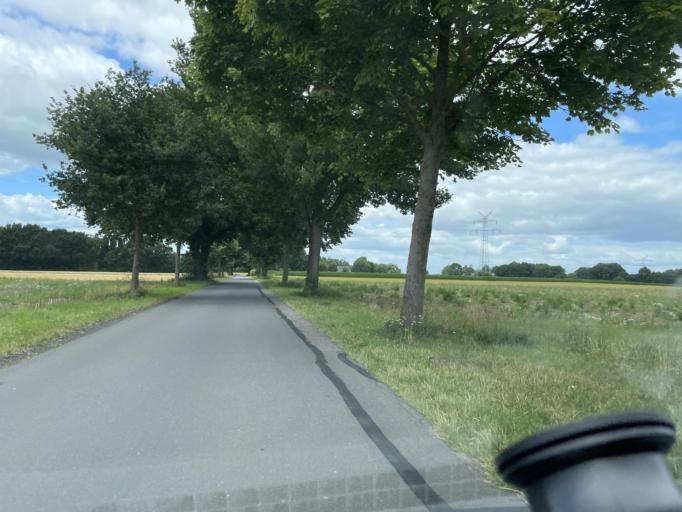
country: DE
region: Lower Saxony
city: Buxtehude
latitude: 53.4517
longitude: 9.7126
